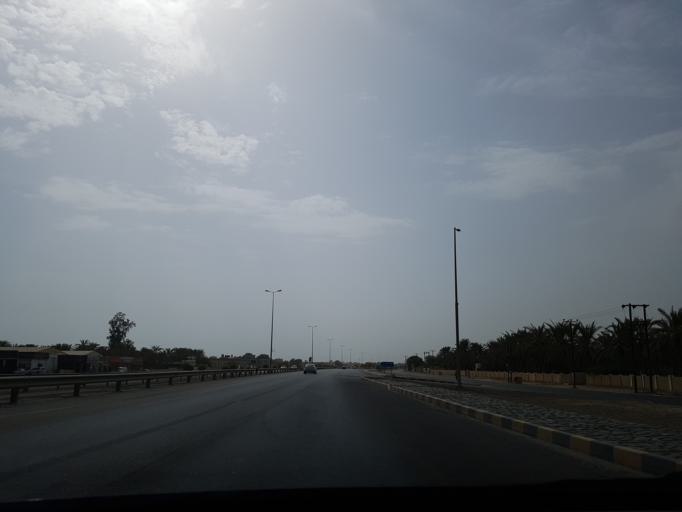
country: OM
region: Al Batinah
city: Saham
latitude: 24.1323
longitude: 56.8901
